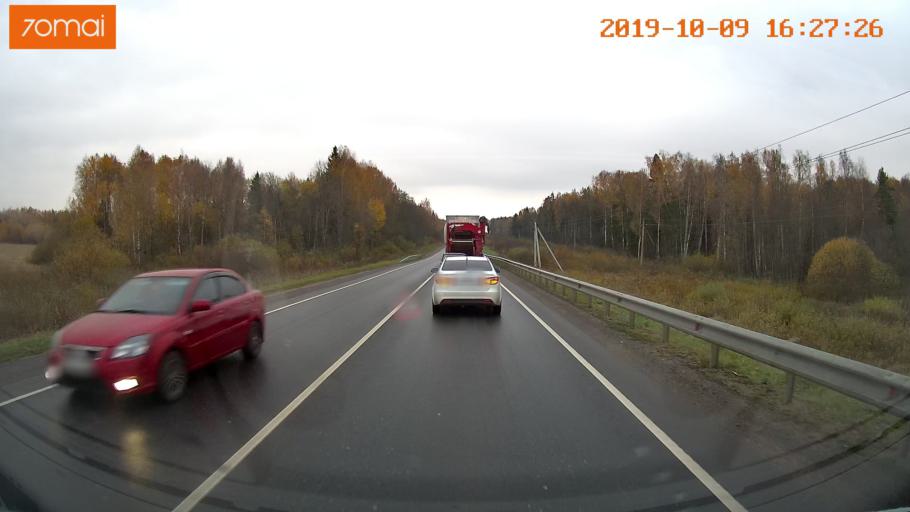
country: RU
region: Kostroma
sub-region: Kostromskoy Rayon
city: Kostroma
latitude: 57.6333
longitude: 40.9280
